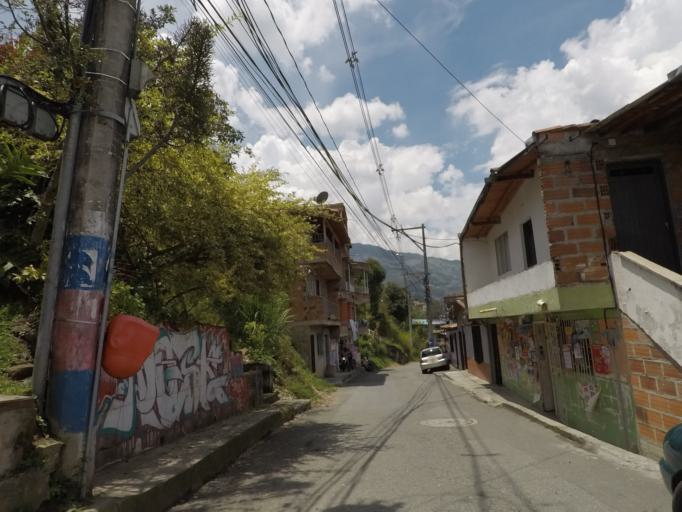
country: CO
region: Antioquia
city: Medellin
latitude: 6.2722
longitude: -75.6312
